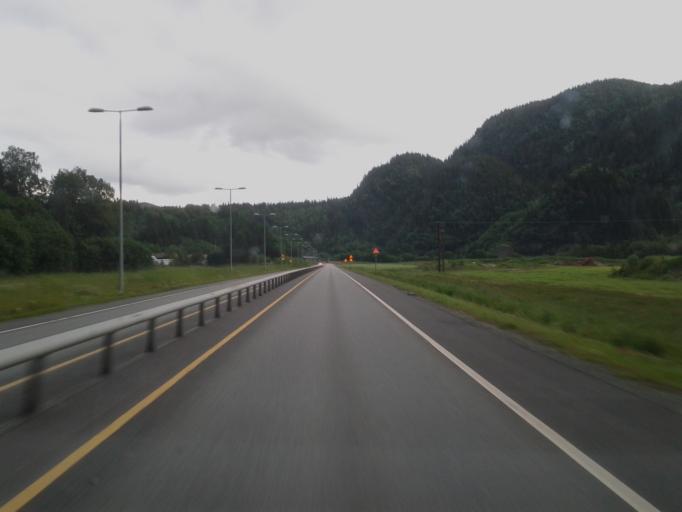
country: NO
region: Sor-Trondelag
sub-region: Midtre Gauldal
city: Storen
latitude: 63.0760
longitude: 10.2618
